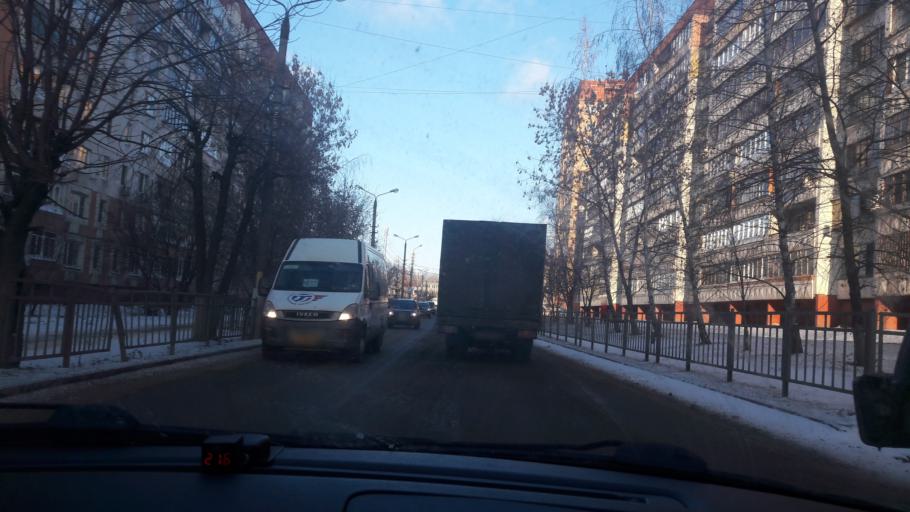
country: RU
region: Tula
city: Tula
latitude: 54.2052
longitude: 37.6450
